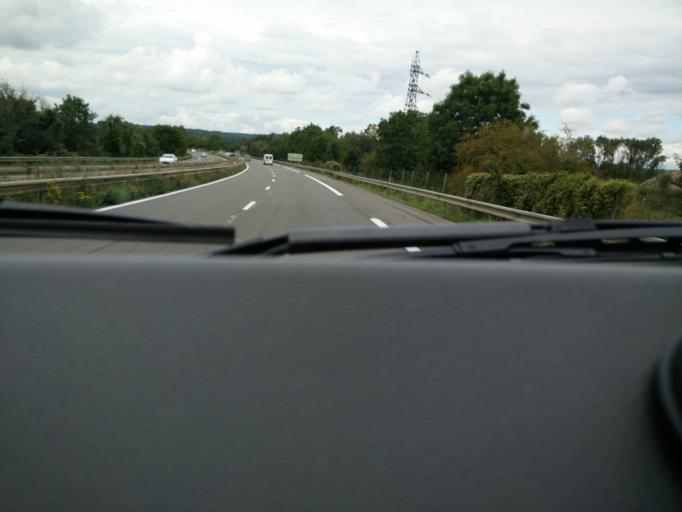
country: FR
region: Champagne-Ardenne
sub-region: Departement des Ardennes
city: Donchery
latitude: 49.7055
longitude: 4.9017
